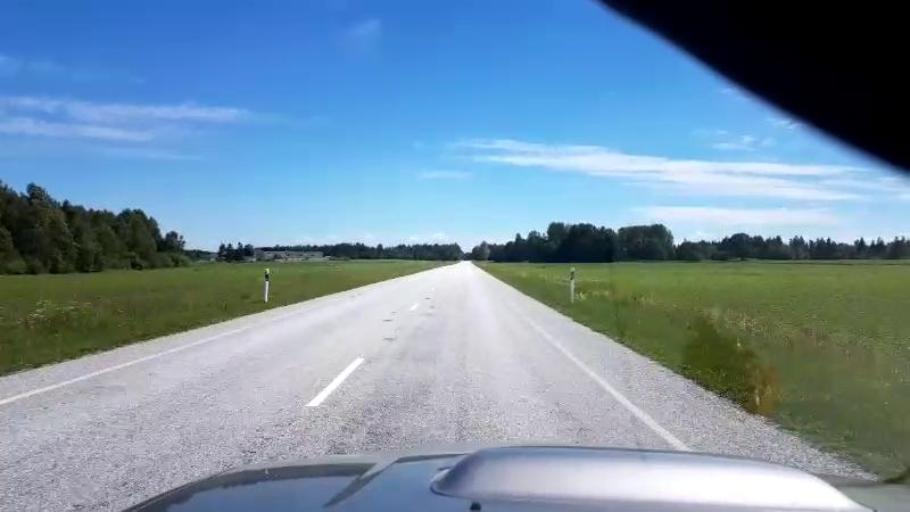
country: EE
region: Laeaene-Virumaa
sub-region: Rakke vald
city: Rakke
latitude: 58.9571
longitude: 26.1696
